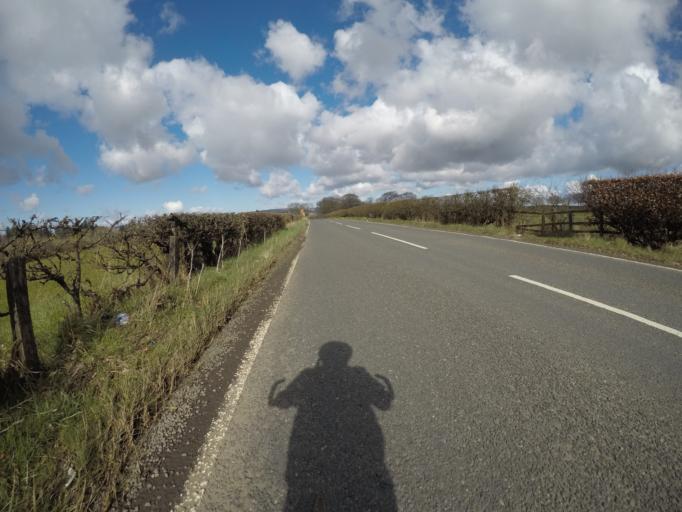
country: GB
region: Scotland
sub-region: North Ayrshire
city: Beith
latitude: 55.7366
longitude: -4.6185
